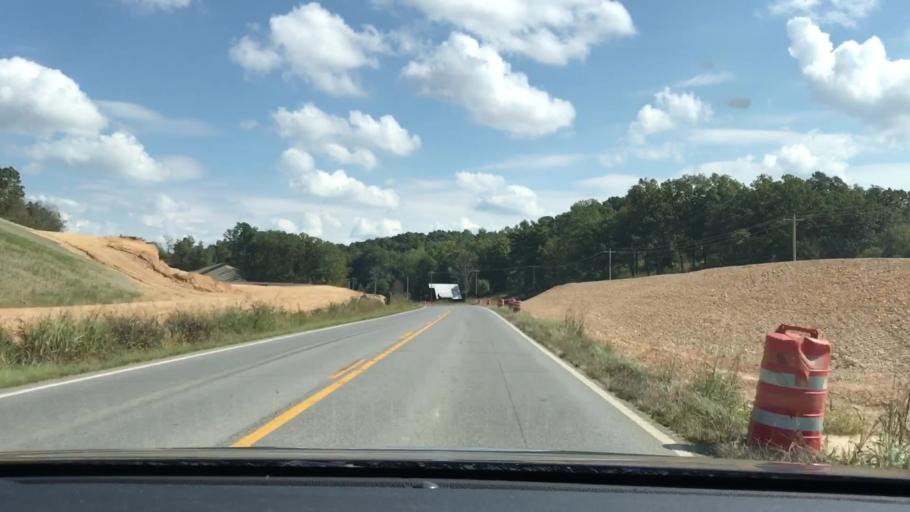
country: US
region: Kentucky
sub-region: Trigg County
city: Cadiz
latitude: 36.8058
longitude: -87.9115
